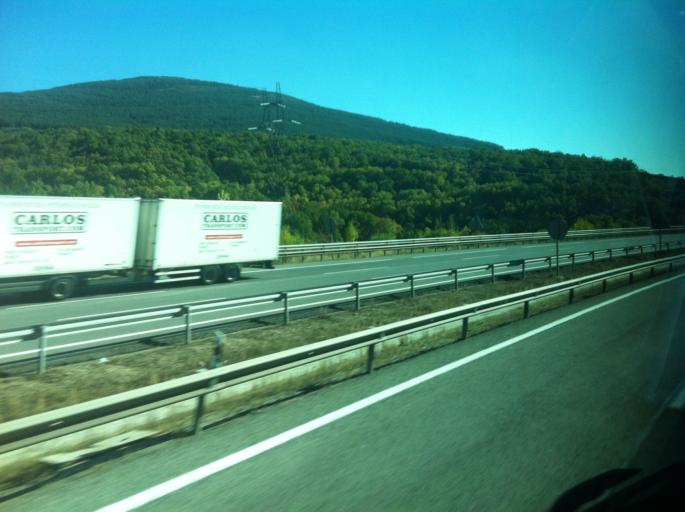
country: ES
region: Madrid
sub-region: Provincia de Madrid
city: Somosierra
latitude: 41.1270
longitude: -3.5833
